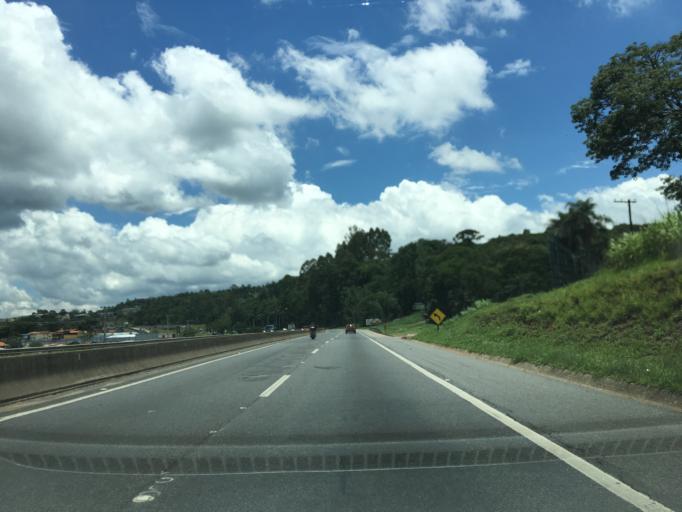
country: BR
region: Sao Paulo
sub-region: Mairipora
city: Mairipora
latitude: -23.2400
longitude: -46.5984
